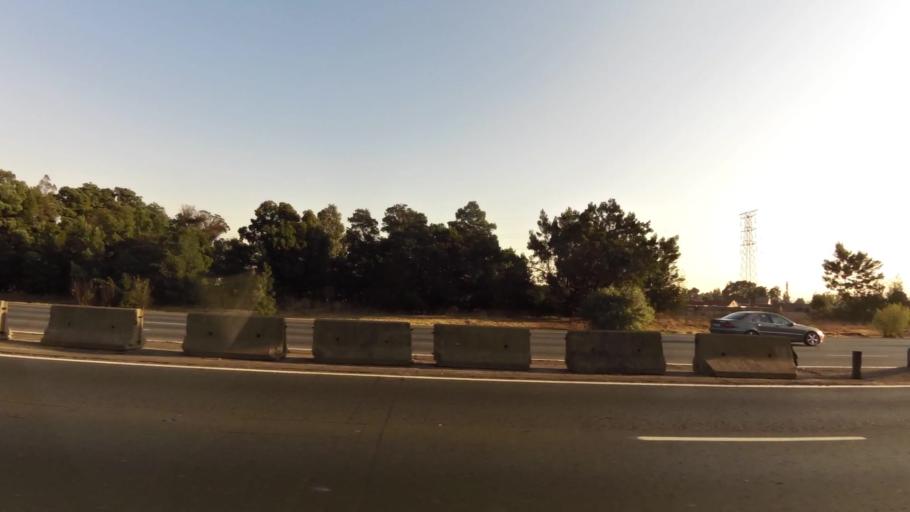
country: ZA
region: Gauteng
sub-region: City of Johannesburg Metropolitan Municipality
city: Johannesburg
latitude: -26.2504
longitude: 27.9985
